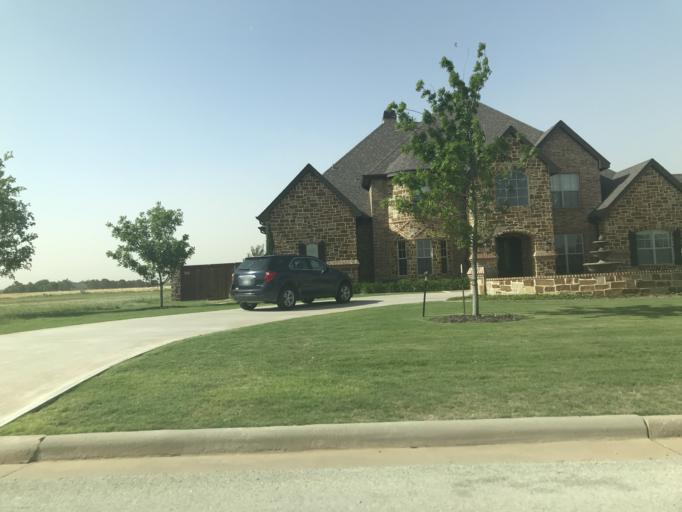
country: US
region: Texas
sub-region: Taylor County
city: Potosi
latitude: 32.3499
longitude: -99.7149
